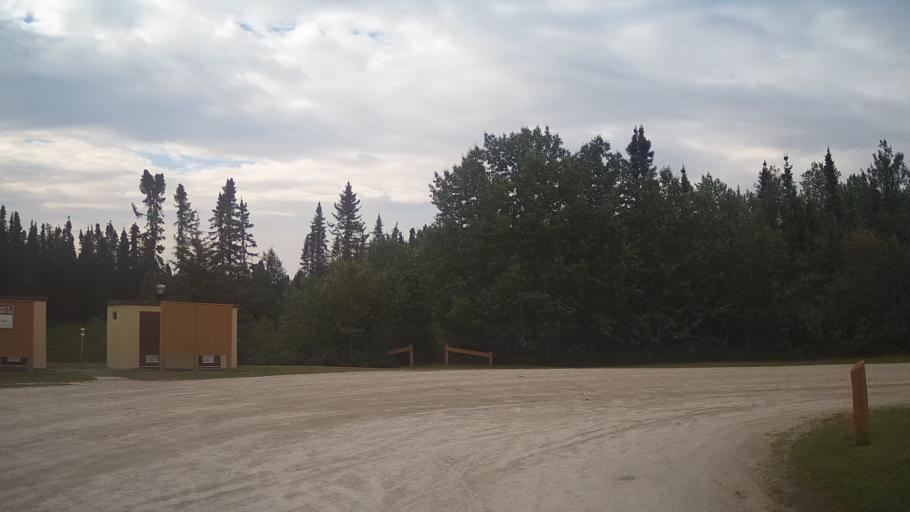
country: CA
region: Ontario
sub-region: Algoma
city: Hornepayne
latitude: 49.7677
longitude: -84.7718
